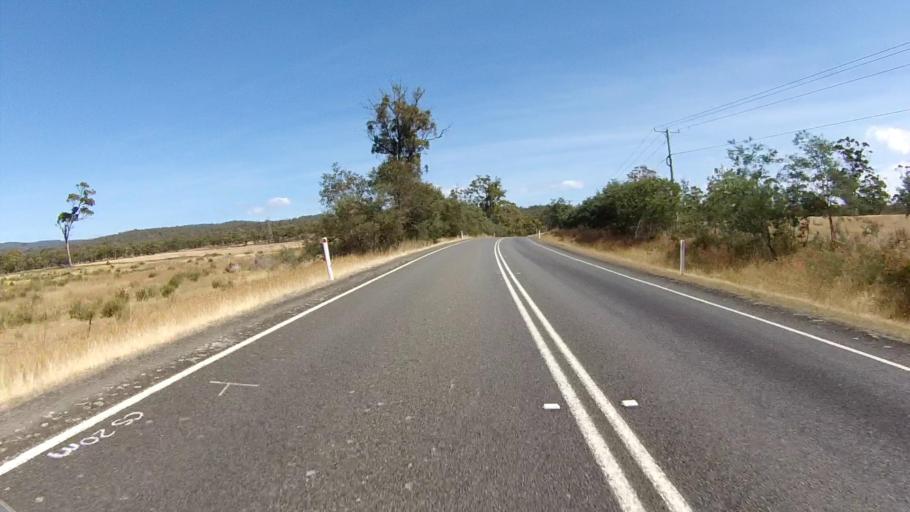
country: AU
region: Tasmania
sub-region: Sorell
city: Sorell
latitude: -42.5782
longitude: 147.8170
